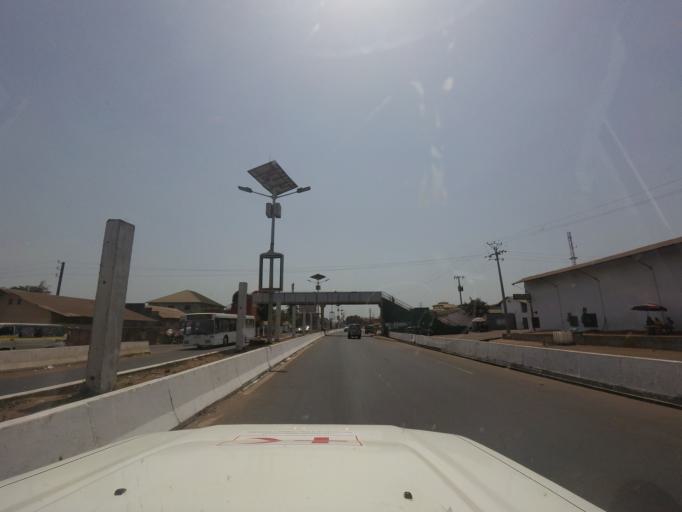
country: GN
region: Conakry
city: Conakry
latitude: 9.5567
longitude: -13.6497
